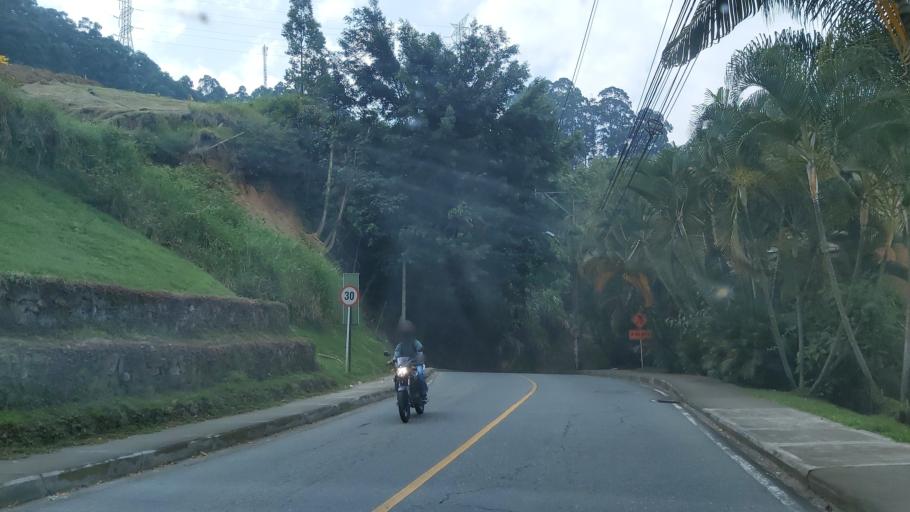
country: CO
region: Antioquia
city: Medellin
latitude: 6.2254
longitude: -75.5601
